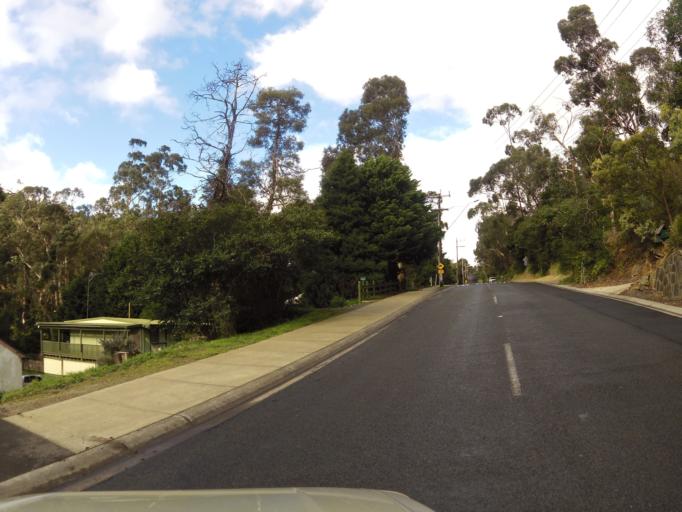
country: AU
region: Victoria
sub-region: Yarra Ranges
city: Tremont
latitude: -37.9002
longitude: 145.3213
